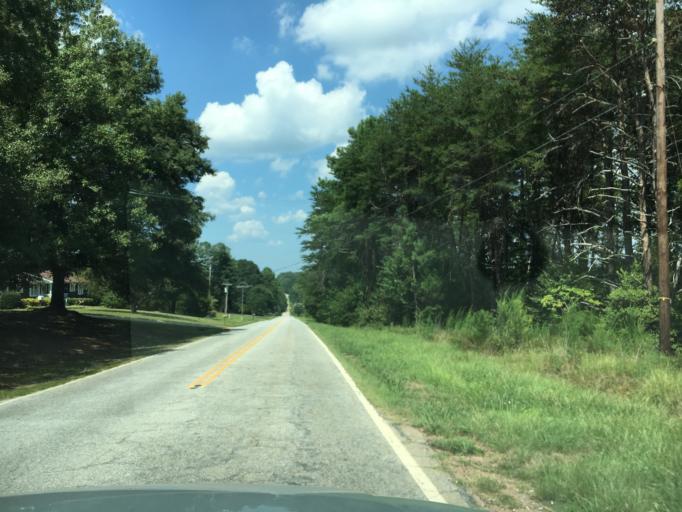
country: US
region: South Carolina
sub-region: Spartanburg County
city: Duncan
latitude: 34.9158
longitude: -82.1318
